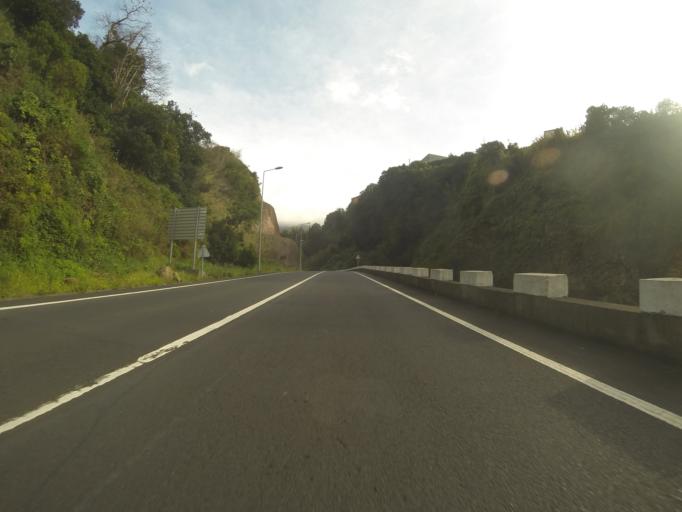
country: PT
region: Madeira
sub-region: Sao Vicente
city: Sao Vicente
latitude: 32.7913
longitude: -17.0341
